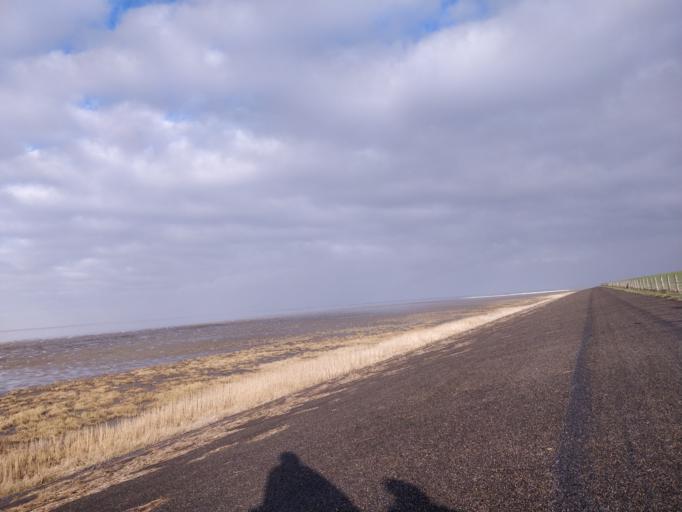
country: NL
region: Friesland
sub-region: Gemeente Het Bildt
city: Sint Jacobiparochie
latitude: 53.3079
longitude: 5.6119
